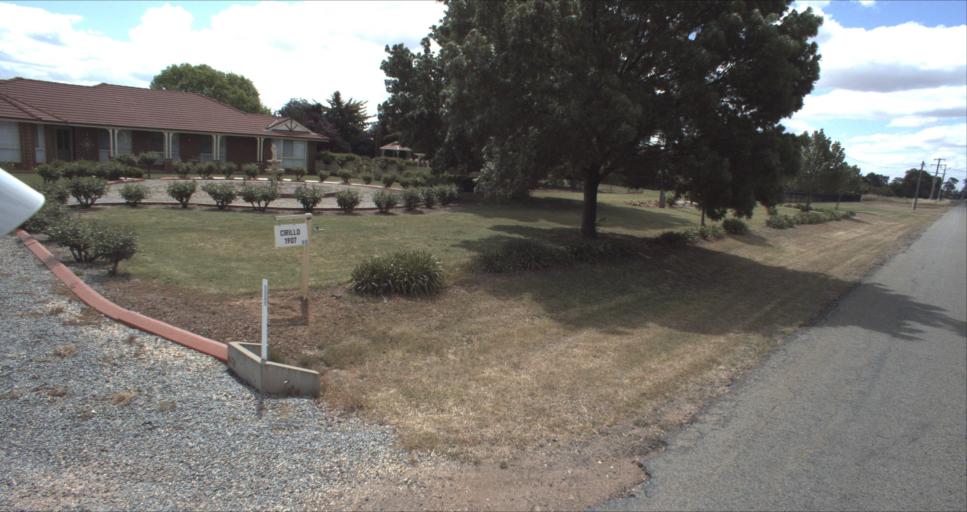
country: AU
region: New South Wales
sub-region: Leeton
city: Leeton
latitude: -34.5854
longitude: 146.3961
